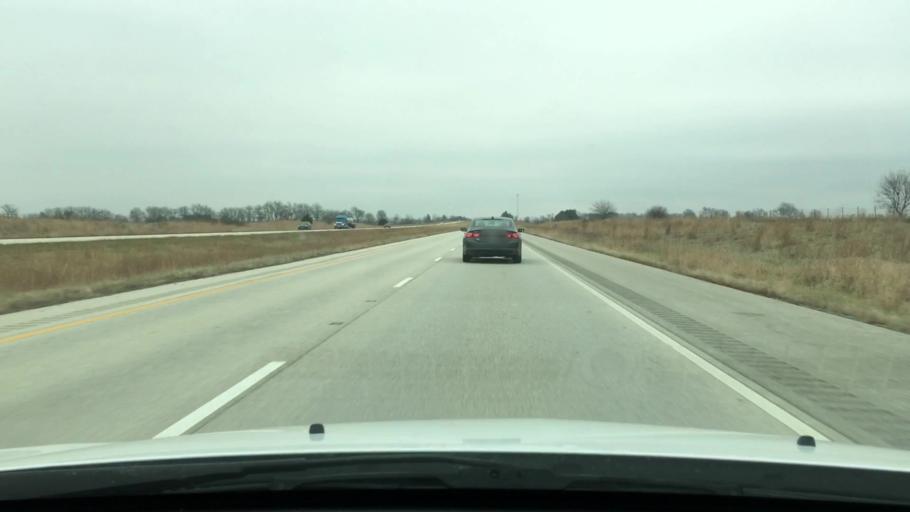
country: US
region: Illinois
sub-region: Sangamon County
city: New Berlin
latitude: 39.7403
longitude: -89.8941
